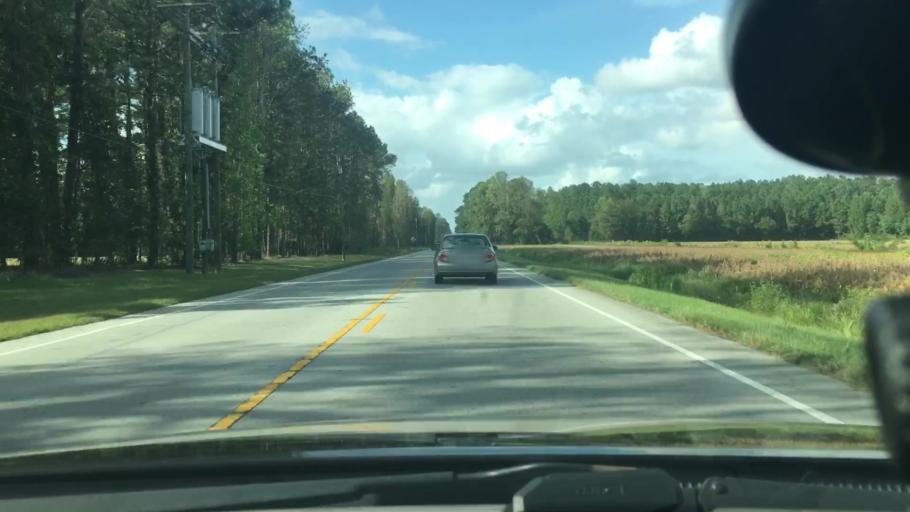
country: US
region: North Carolina
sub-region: Craven County
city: New Bern
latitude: 35.1971
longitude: -77.0552
